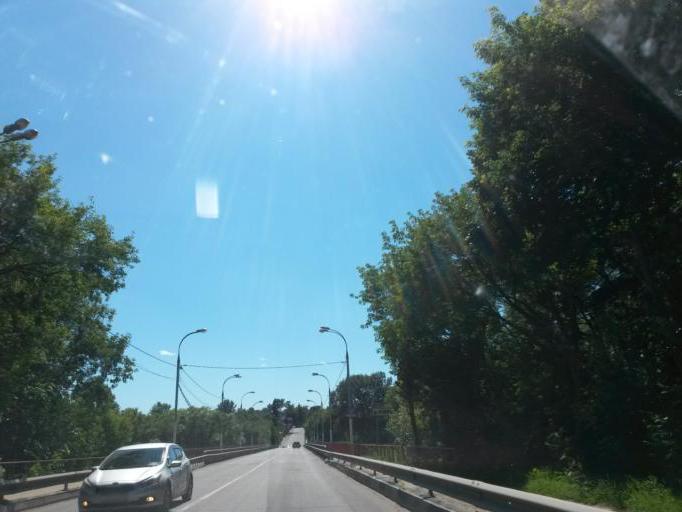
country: RU
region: Moskovskaya
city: Serpukhov
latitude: 54.9161
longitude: 37.4008
